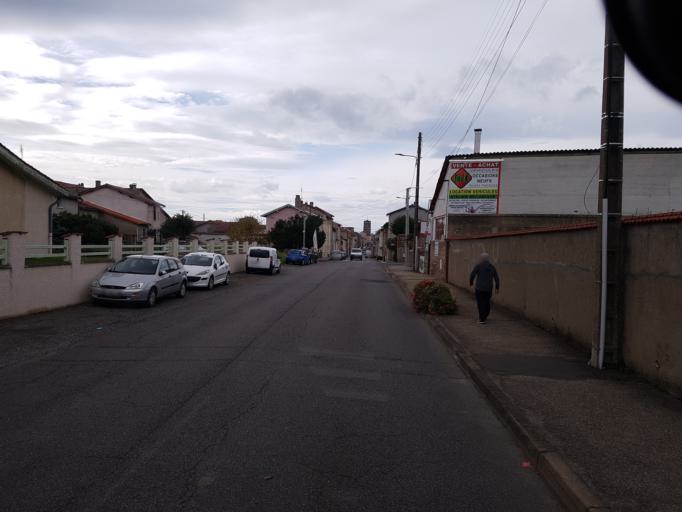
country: FR
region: Rhone-Alpes
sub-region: Departement de la Loire
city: Chazelles-sur-Lyon
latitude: 45.6419
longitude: 4.3964
